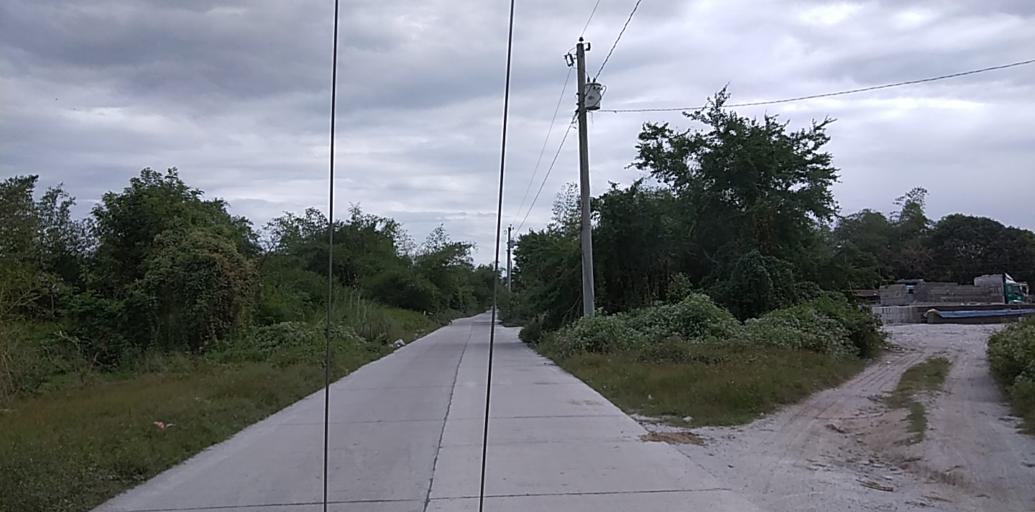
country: PH
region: Central Luzon
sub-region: Province of Pampanga
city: Pulung Santol
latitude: 15.0568
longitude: 120.5574
